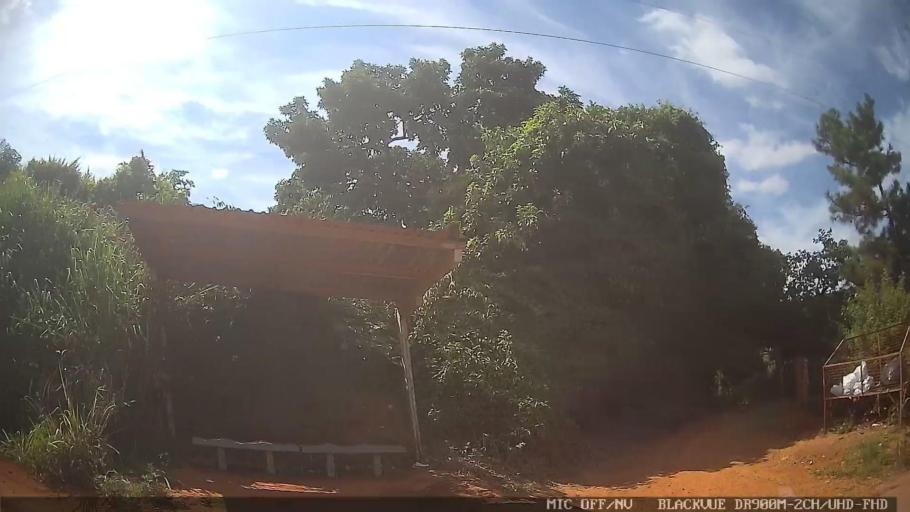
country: BR
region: Sao Paulo
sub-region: Braganca Paulista
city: Braganca Paulista
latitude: -22.9887
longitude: -46.6495
